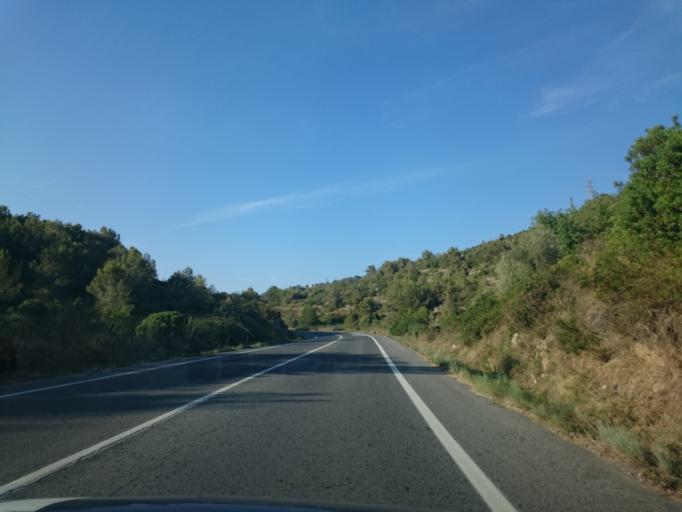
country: ES
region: Catalonia
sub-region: Provincia de Barcelona
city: Vilanova i la Geltru
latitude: 41.2589
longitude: 1.7164
